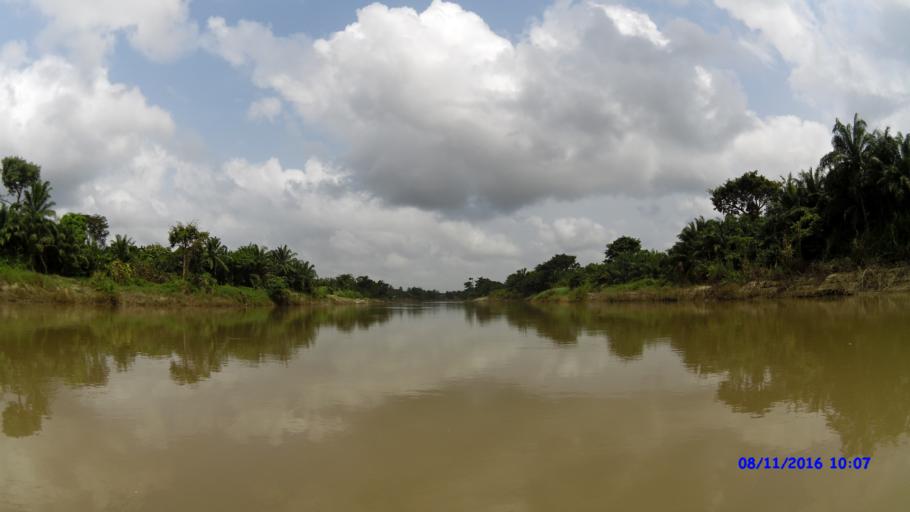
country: BJ
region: Mono
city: Come
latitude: 6.4495
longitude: 1.7539
